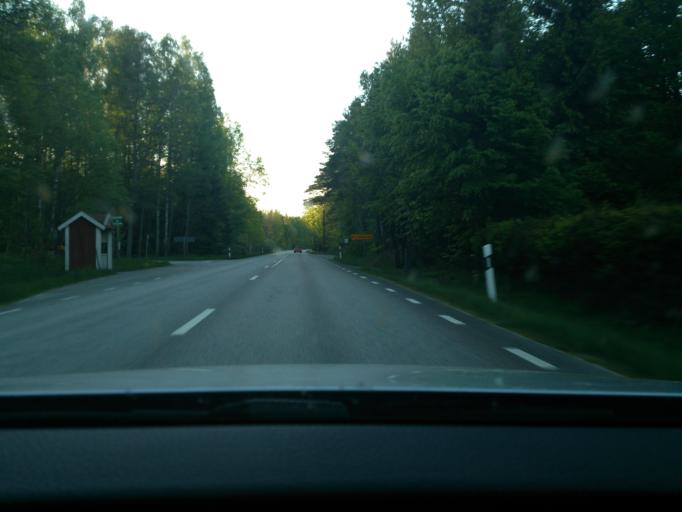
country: SE
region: Kronoberg
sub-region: Vaxjo Kommun
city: Gemla
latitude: 56.9623
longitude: 14.7128
